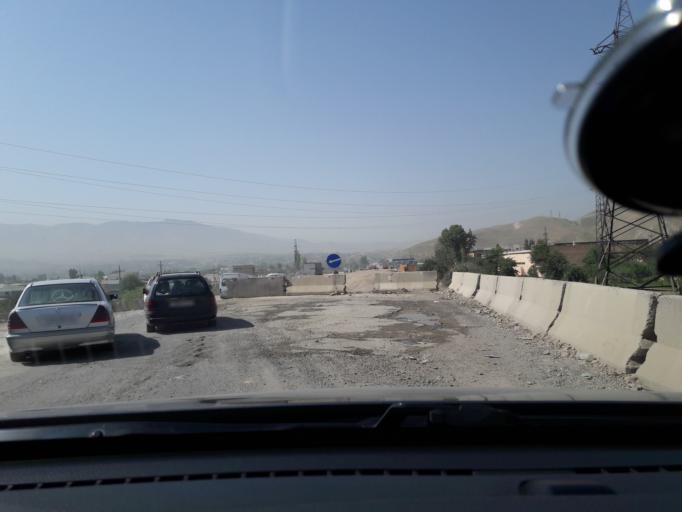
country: TJ
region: Dushanbe
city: Boshkengash
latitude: 38.4569
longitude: 68.7361
